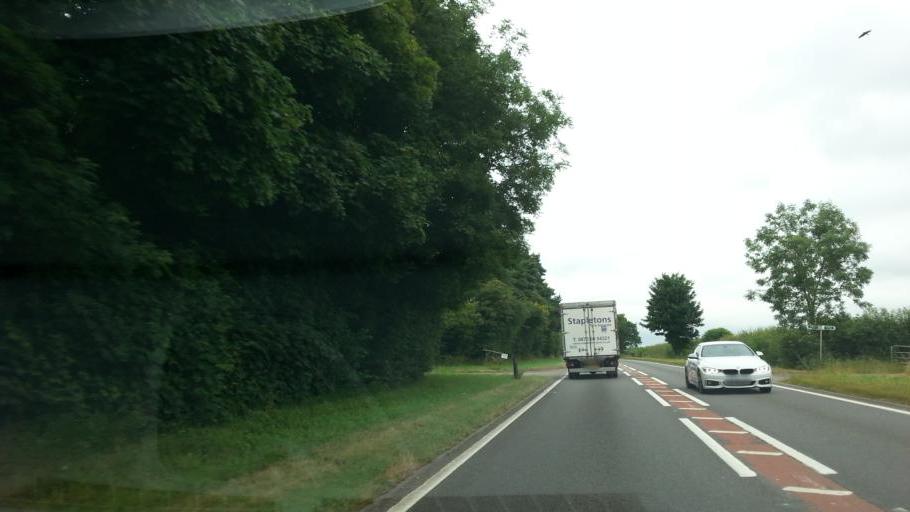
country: GB
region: England
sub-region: Northamptonshire
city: Northampton
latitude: 52.3026
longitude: -0.8237
